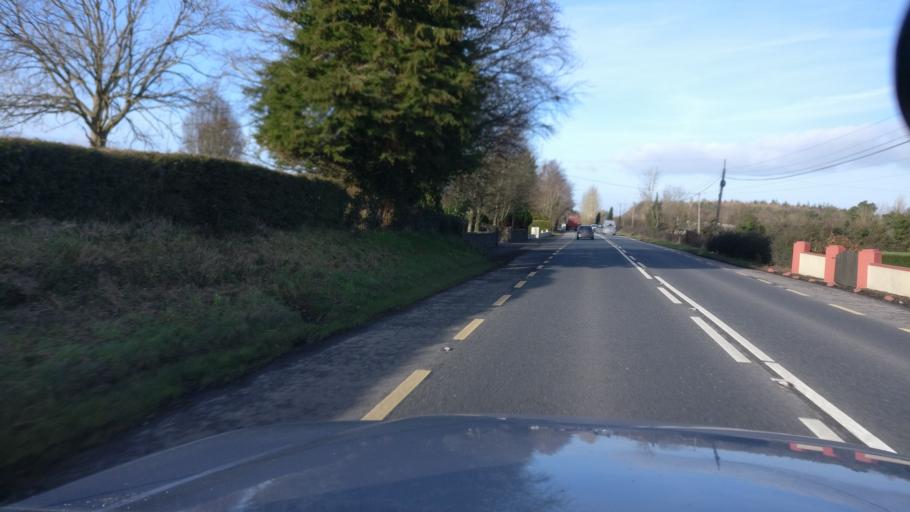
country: IE
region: Leinster
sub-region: Uibh Fhaili
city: Tullamore
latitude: 53.2235
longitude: -7.4759
